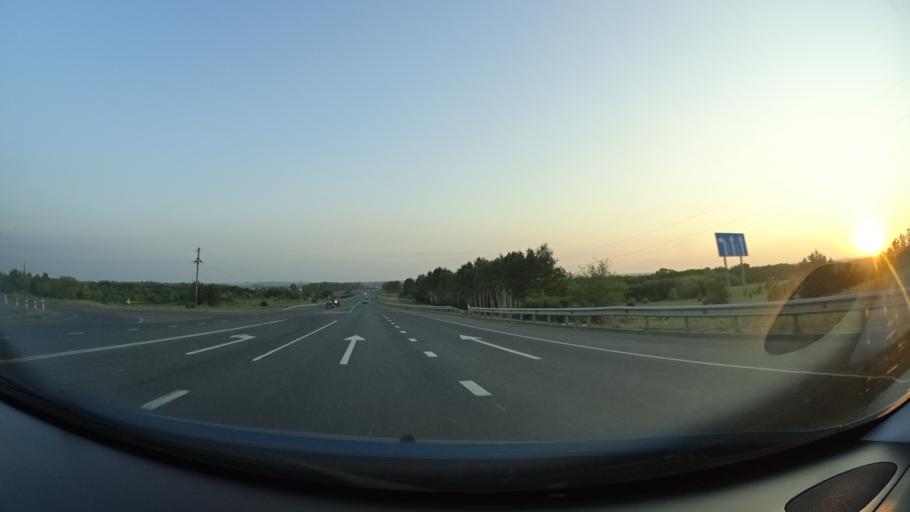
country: RU
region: Samara
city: Sernovodsk
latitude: 53.8987
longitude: 51.2738
